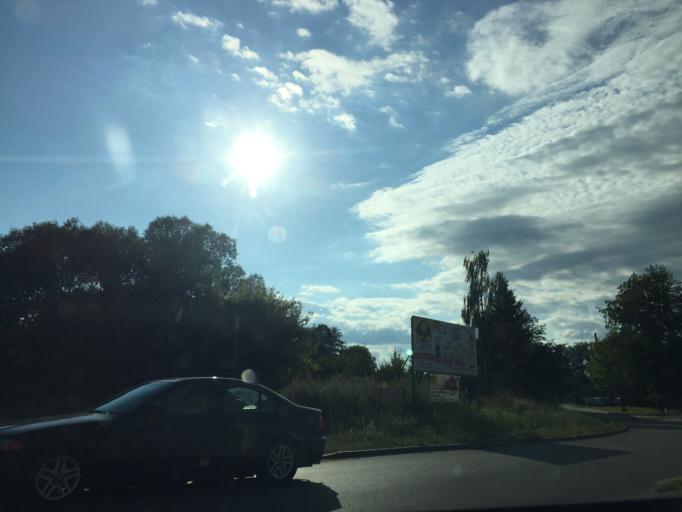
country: PL
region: Podlasie
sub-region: Powiat grajewski
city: Rajgrod
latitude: 53.7294
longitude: 22.6855
